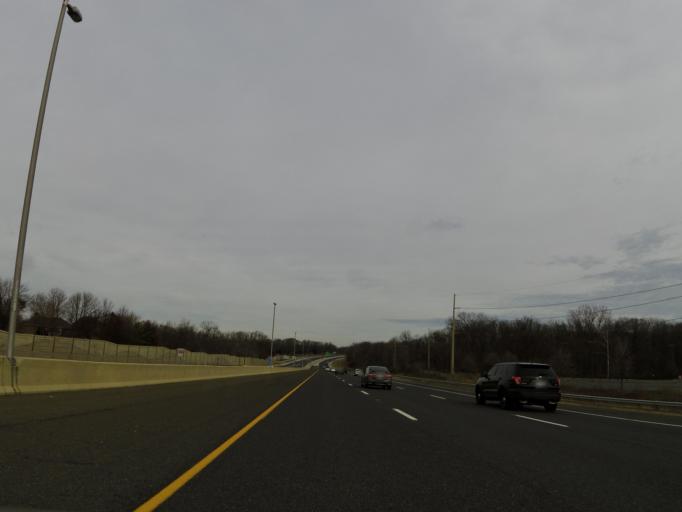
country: US
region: Indiana
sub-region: Boone County
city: Zionsville
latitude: 39.9132
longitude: -86.2697
